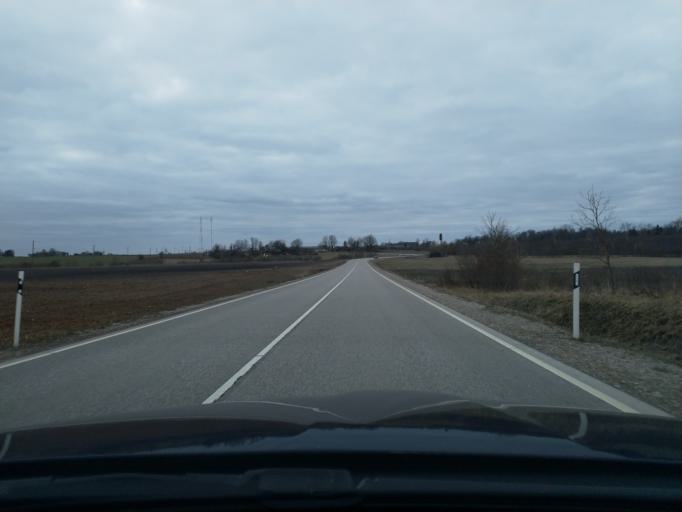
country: LV
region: Talsu Rajons
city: Sabile
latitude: 56.9435
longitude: 22.4154
